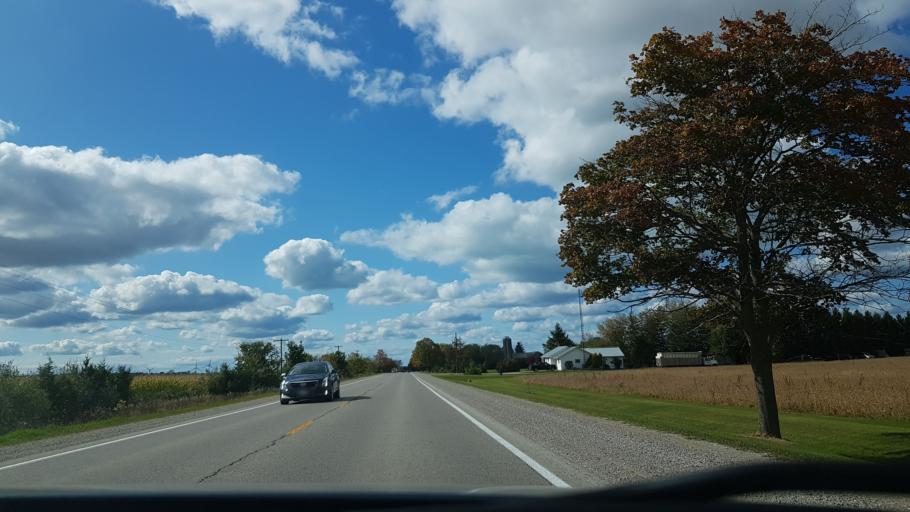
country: CA
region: Ontario
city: Bluewater
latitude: 43.3420
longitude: -81.6739
